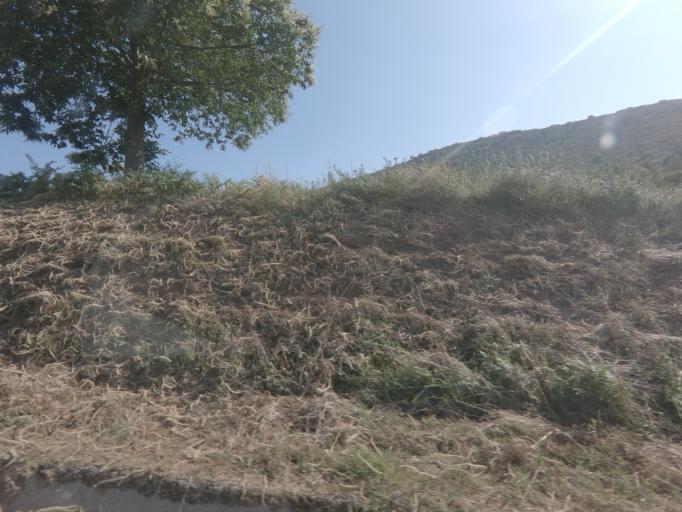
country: PT
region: Vila Real
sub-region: Sabrosa
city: Vilela
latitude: 41.2307
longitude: -7.5696
